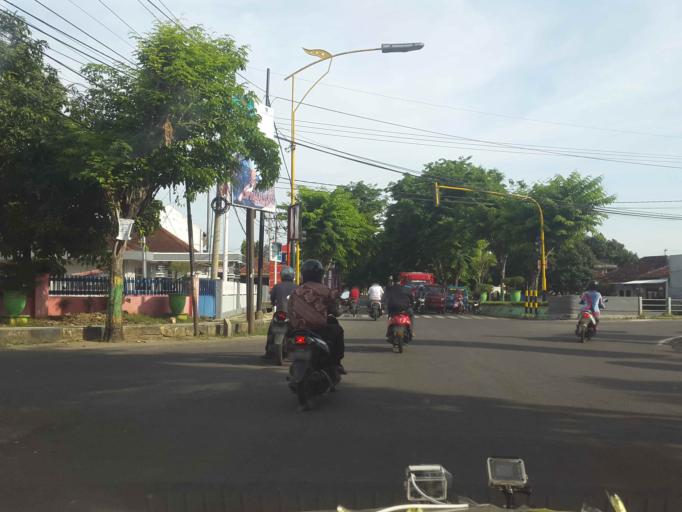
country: ID
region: East Java
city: Sumenep
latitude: -7.0131
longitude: 113.8690
